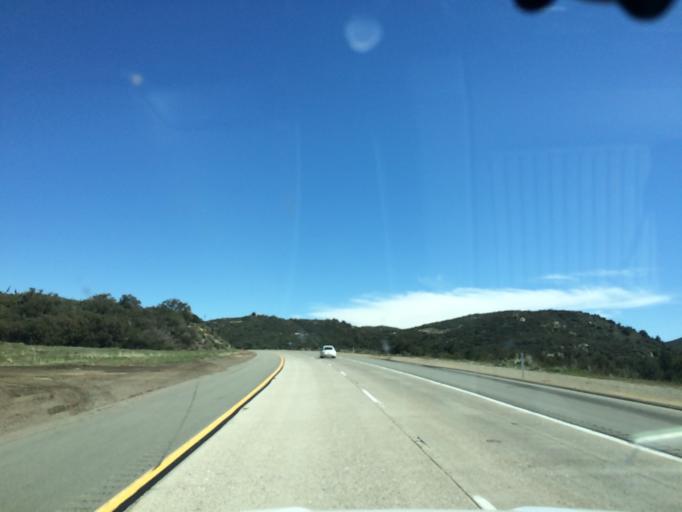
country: US
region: California
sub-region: San Diego County
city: Pine Valley
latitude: 32.8186
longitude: -116.5462
